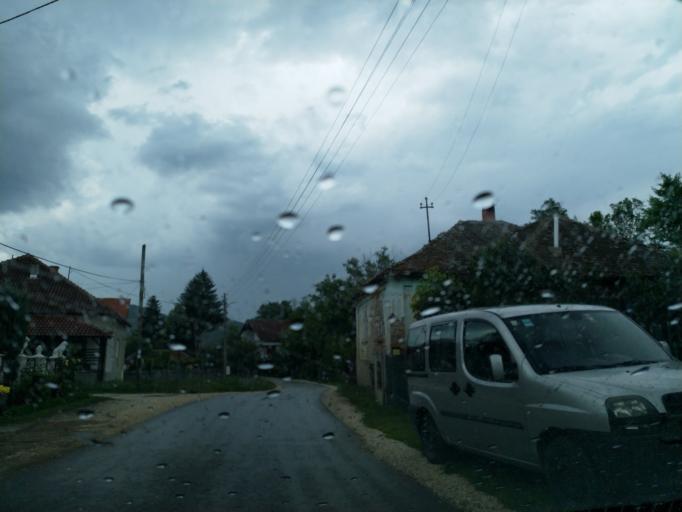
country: RS
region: Central Serbia
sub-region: Borski Okrug
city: Bor
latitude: 44.0117
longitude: 21.9844
